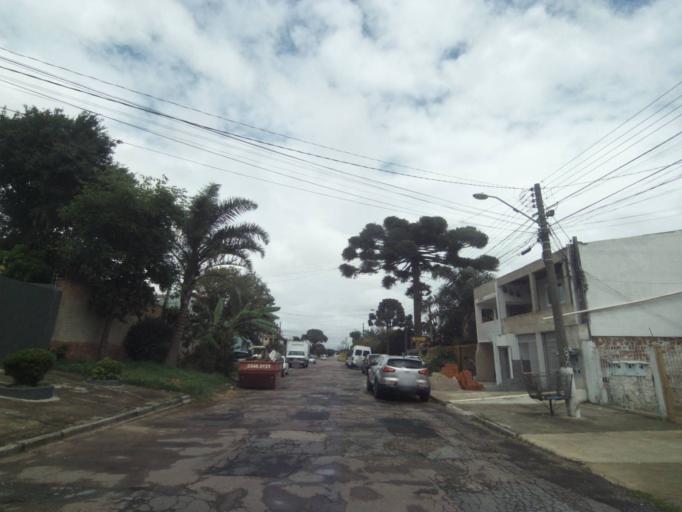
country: BR
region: Parana
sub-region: Curitiba
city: Curitiba
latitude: -25.4881
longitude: -49.3029
